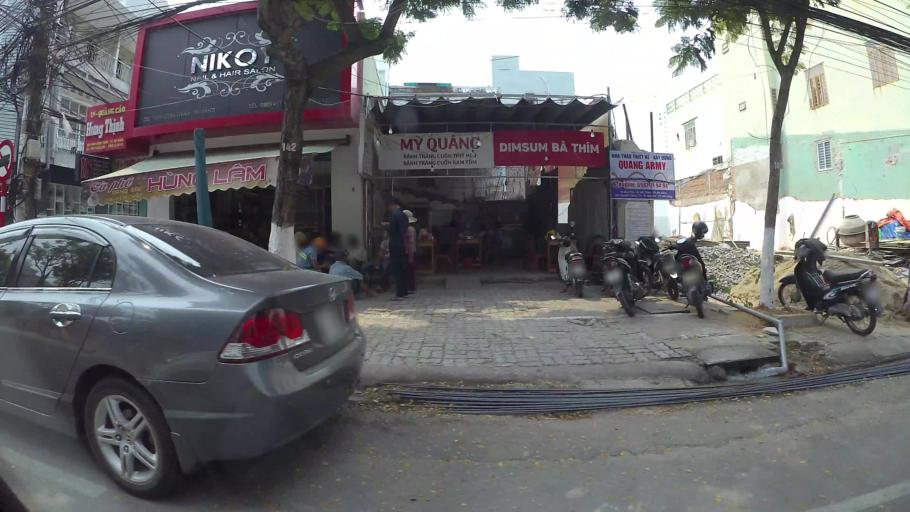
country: VN
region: Da Nang
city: Da Nang
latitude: 16.0588
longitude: 108.2192
